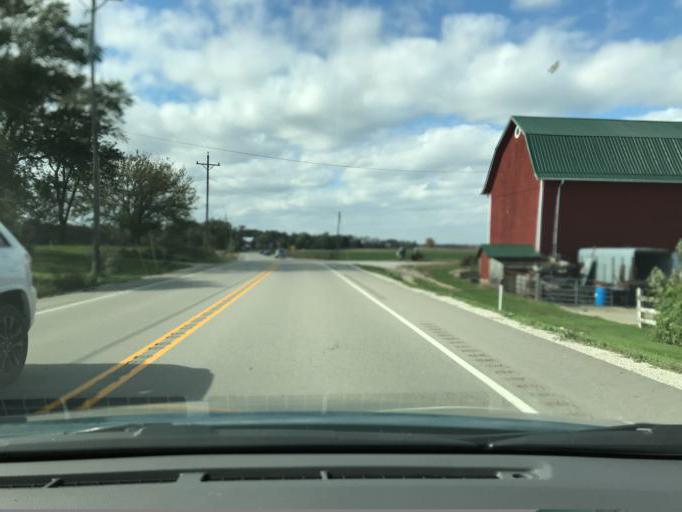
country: US
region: Wisconsin
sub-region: Racine County
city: Browns Lake
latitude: 42.6567
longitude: -88.2282
